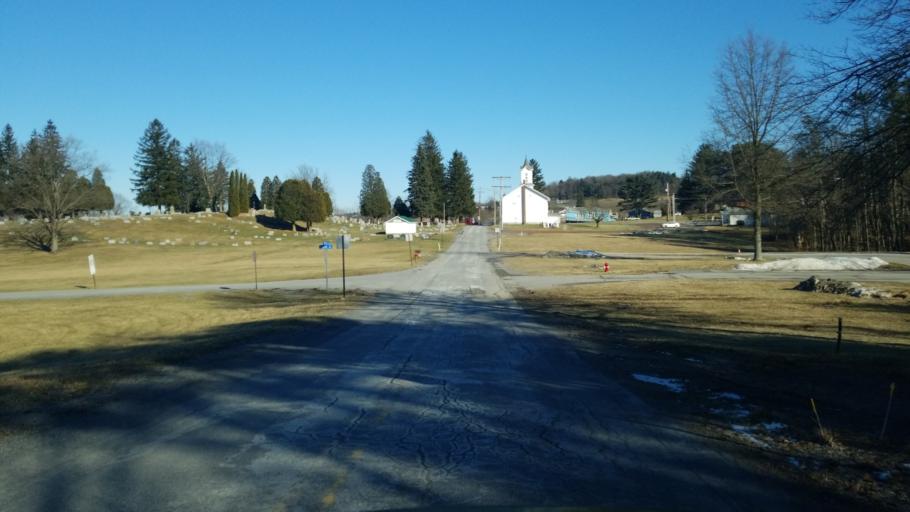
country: US
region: Pennsylvania
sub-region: Clearfield County
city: Sandy
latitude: 41.0539
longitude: -78.7257
